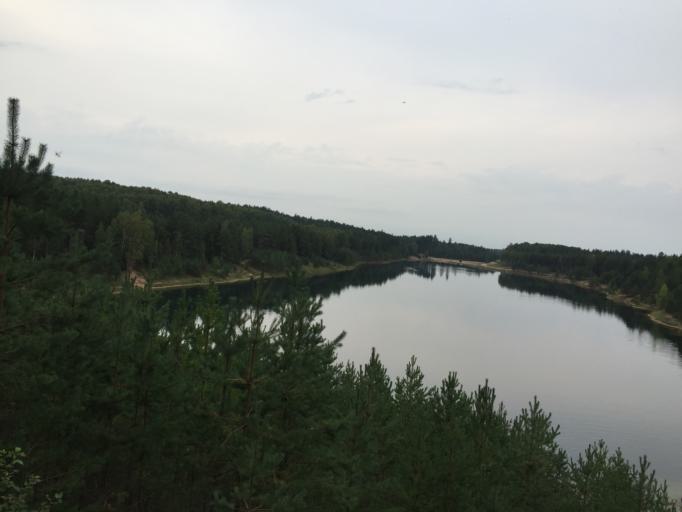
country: LV
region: Ikskile
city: Ikskile
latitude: 56.8372
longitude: 24.5586
